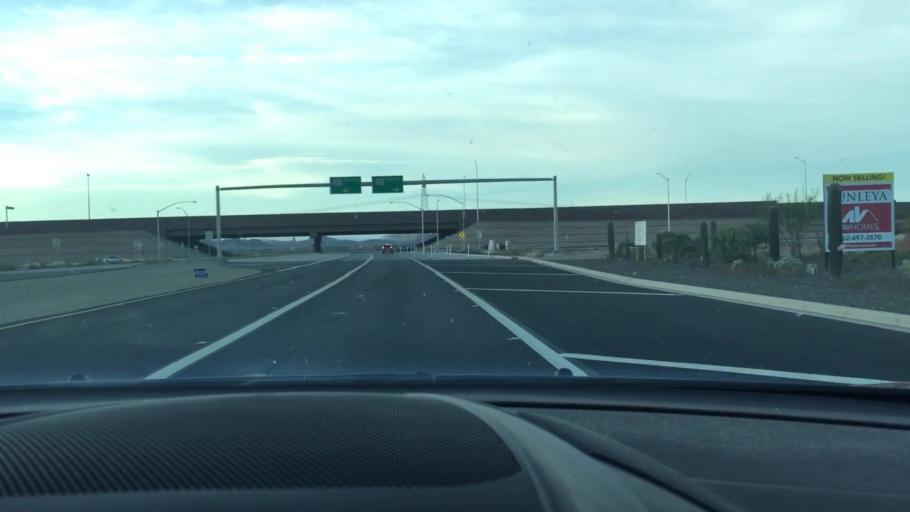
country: US
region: Arizona
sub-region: Maricopa County
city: Sun City West
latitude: 33.6962
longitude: -112.3338
